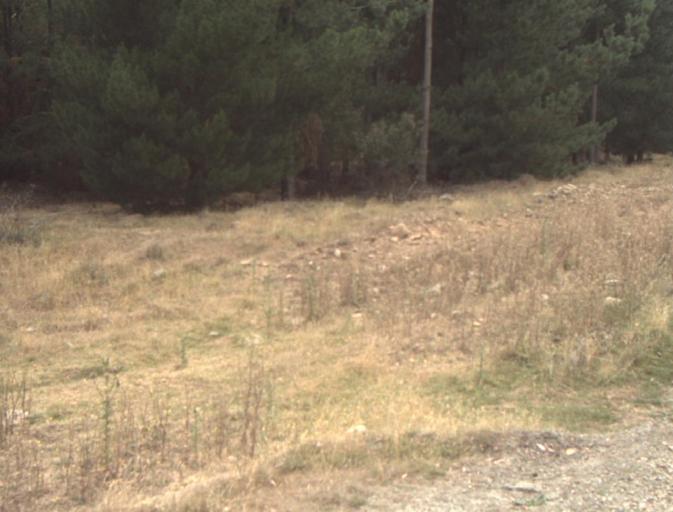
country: AU
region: Tasmania
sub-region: Dorset
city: Scottsdale
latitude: -41.4714
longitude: 147.6248
